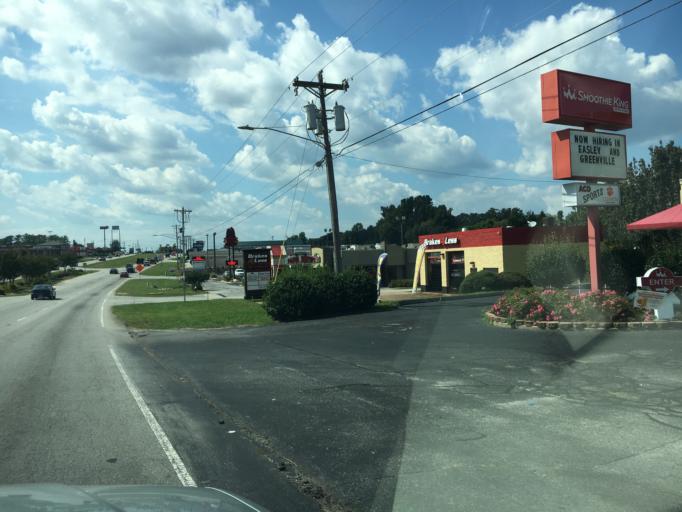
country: US
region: South Carolina
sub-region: Pickens County
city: Easley
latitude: 34.8247
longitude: -82.5580
